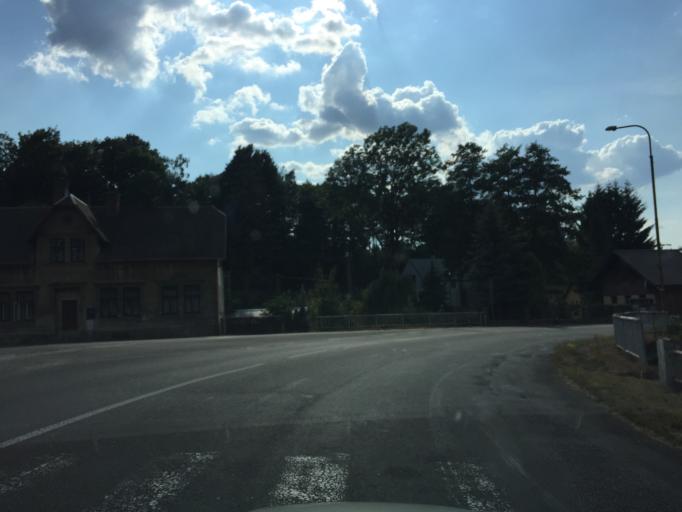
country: CZ
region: Liberecky
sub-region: Okres Jablonec nad Nisou
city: Jablonec nad Nisou
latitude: 50.6792
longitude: 15.1632
